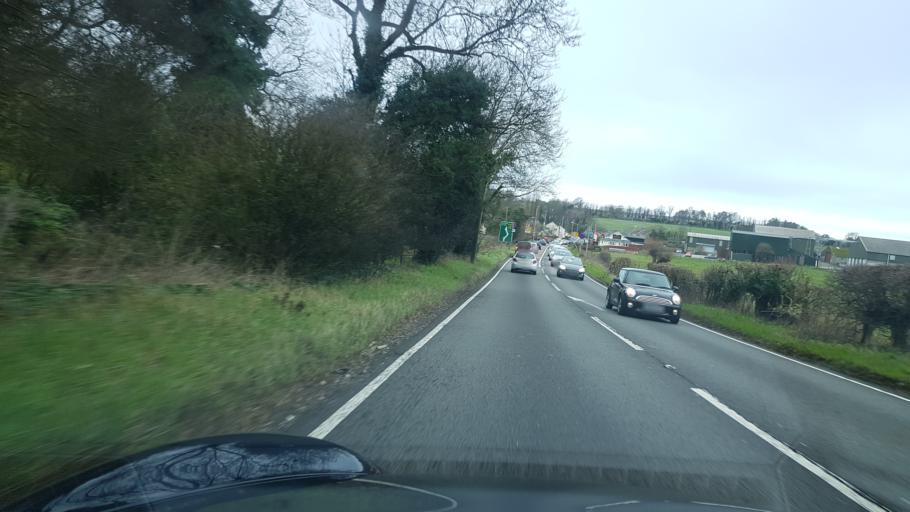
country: GB
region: England
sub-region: Wiltshire
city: Winterbourne Stoke
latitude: 51.1696
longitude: -1.8867
